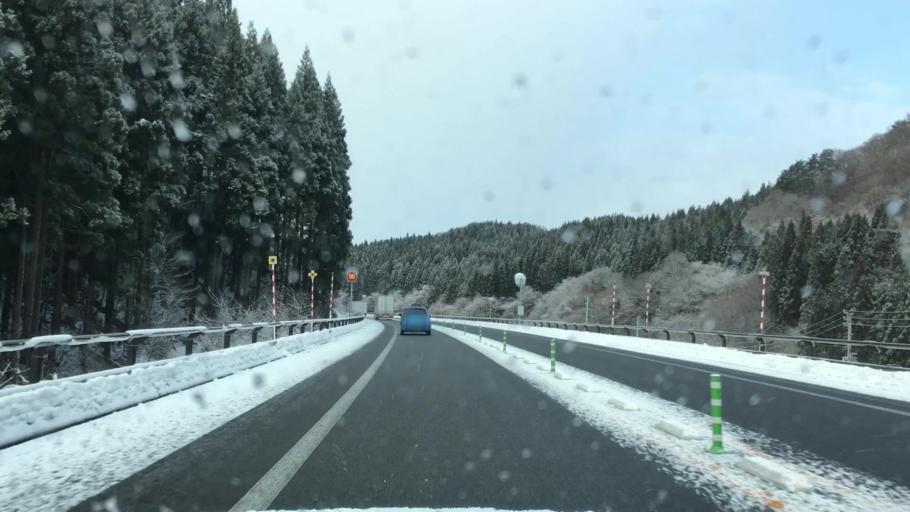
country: JP
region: Akita
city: Takanosu
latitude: 40.2264
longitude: 140.4459
